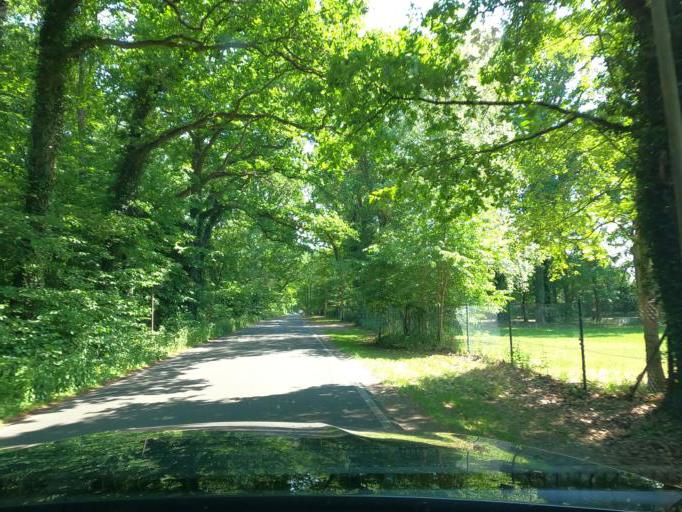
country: DE
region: Lower Saxony
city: Isernhagen Farster Bauerschaft
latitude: 52.4048
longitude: 9.8548
